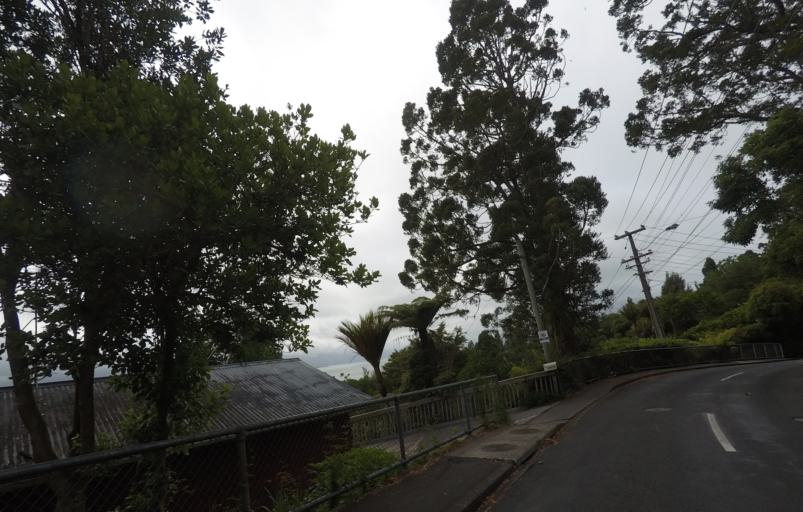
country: NZ
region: Auckland
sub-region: Auckland
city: Titirangi
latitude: -36.9423
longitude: 174.6600
